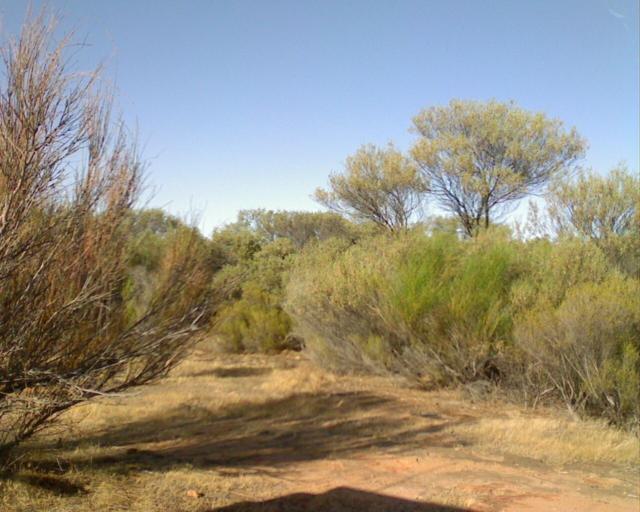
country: AU
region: Western Australia
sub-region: Wongan-Ballidu
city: Wongan Hills
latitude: -30.2919
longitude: 116.9651
